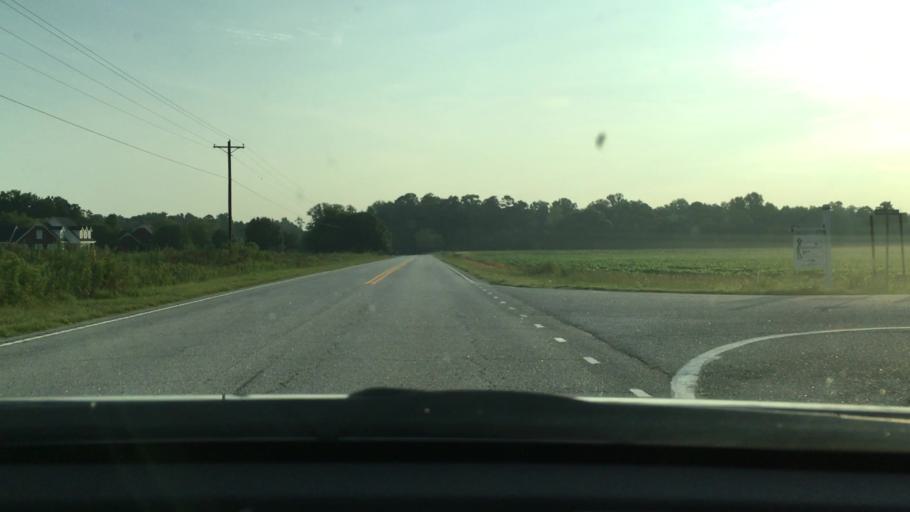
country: US
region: South Carolina
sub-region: Florence County
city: Timmonsville
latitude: 34.1872
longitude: -80.0460
